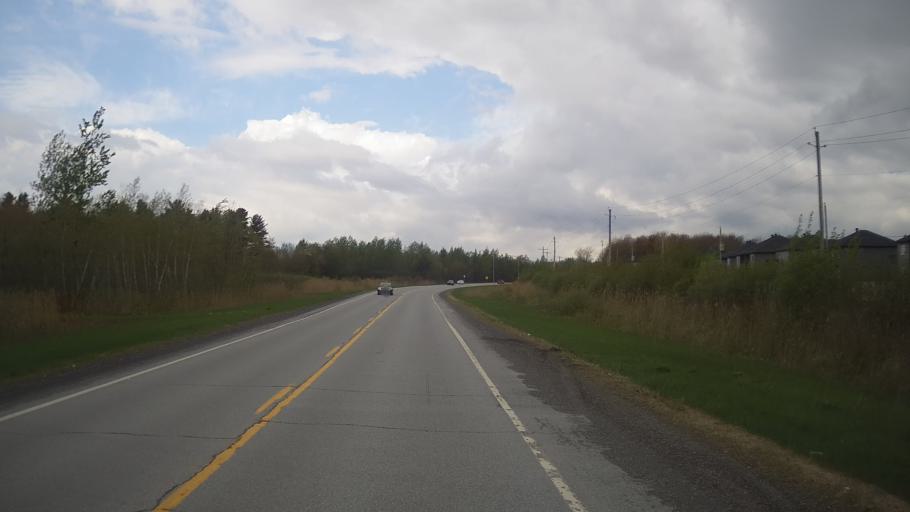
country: CA
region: Quebec
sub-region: Monteregie
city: Farnham
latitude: 45.2706
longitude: -72.9583
